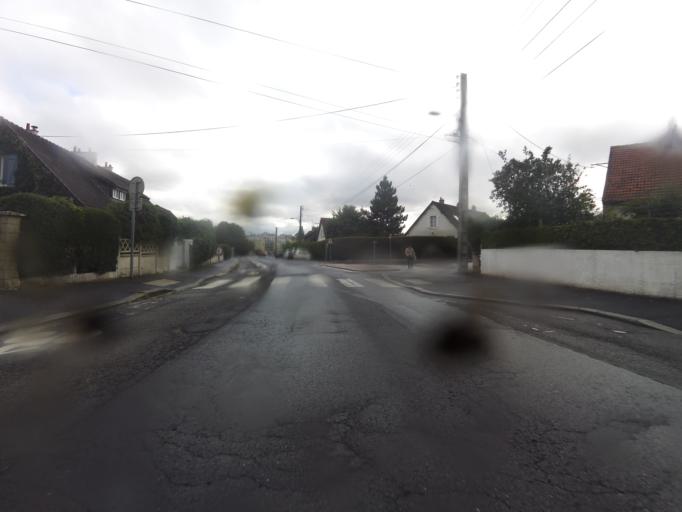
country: FR
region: Lower Normandy
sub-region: Departement du Calvados
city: Caen
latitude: 49.1938
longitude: -0.3575
